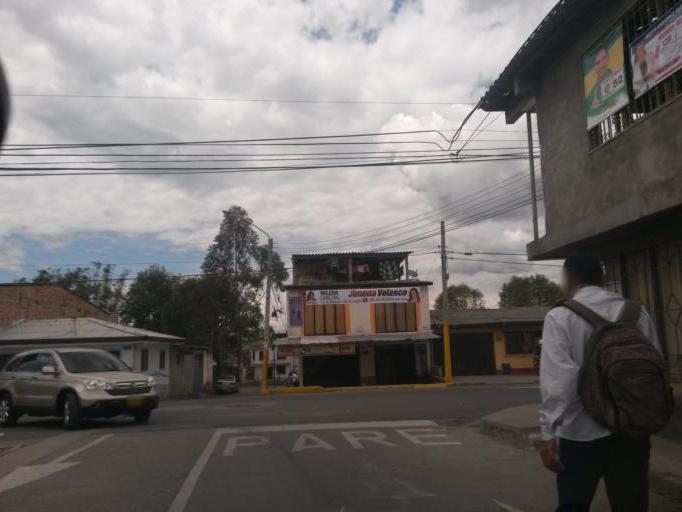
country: CO
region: Cauca
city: Popayan
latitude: 2.4476
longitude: -76.6251
